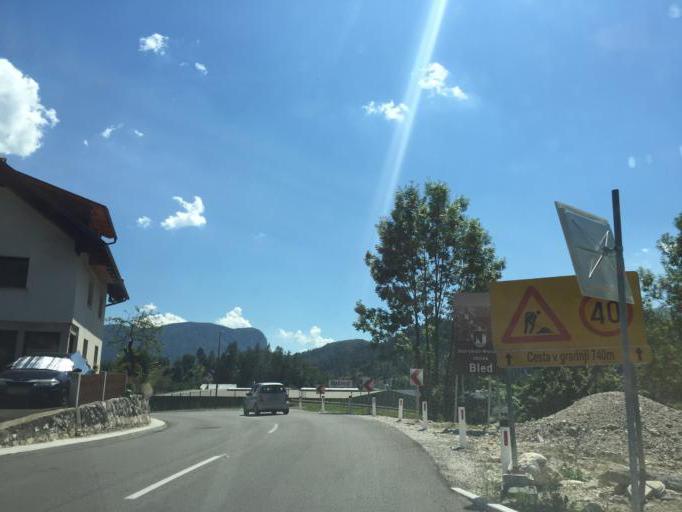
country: SI
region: Gorje
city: Zgornje Gorje
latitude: 46.3797
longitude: 14.0872
